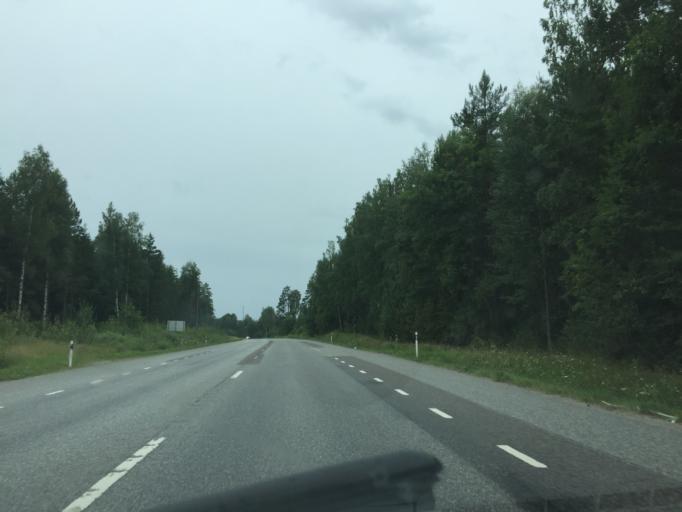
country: SE
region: OErebro
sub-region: Orebro Kommun
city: Orebro
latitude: 59.2300
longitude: 15.2272
